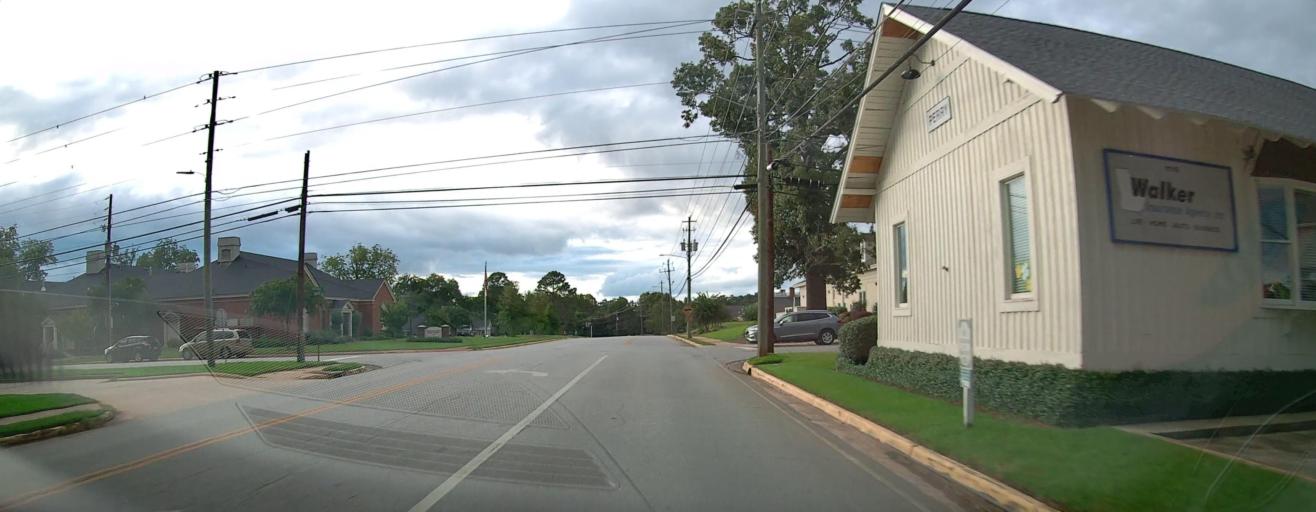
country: US
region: Georgia
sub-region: Houston County
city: Perry
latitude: 32.4605
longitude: -83.7329
